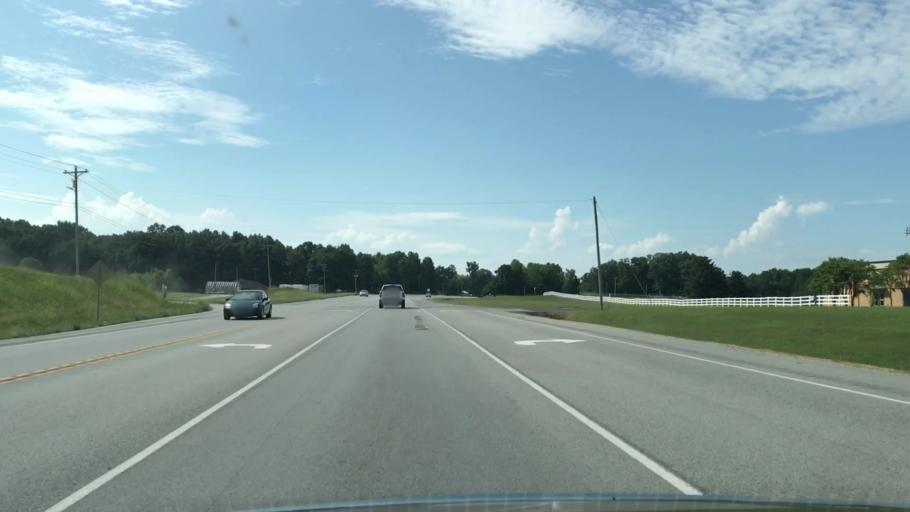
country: US
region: Kentucky
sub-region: Allen County
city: Scottsville
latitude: 36.7538
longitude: -86.2136
